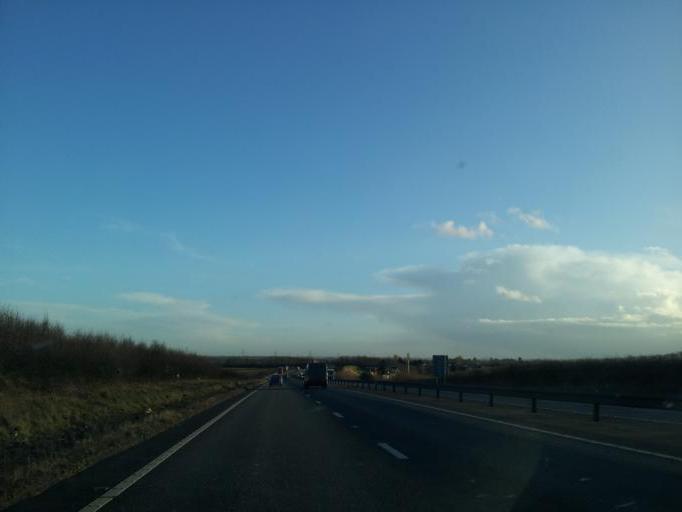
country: GB
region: England
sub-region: Nottinghamshire
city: Newark on Trent
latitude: 53.0703
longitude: -0.7672
